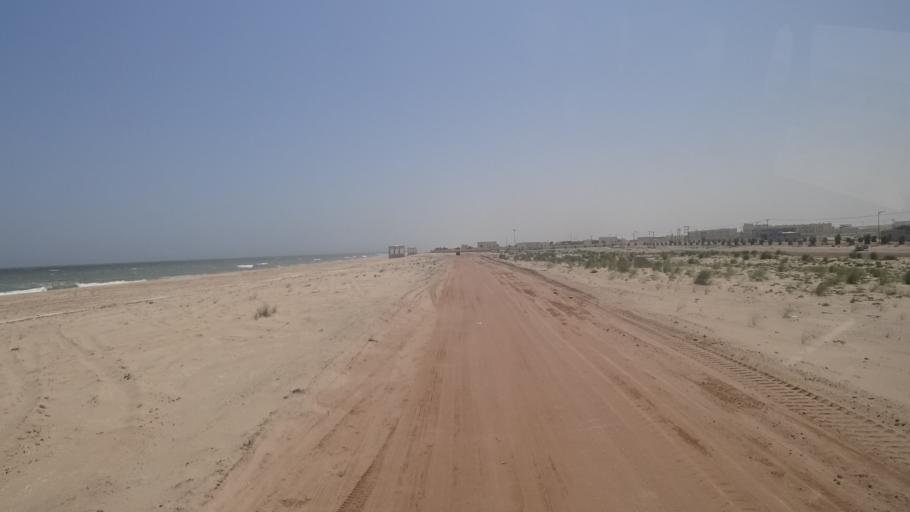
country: OM
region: Ash Sharqiyah
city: Sur
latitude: 21.8247
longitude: 59.5558
